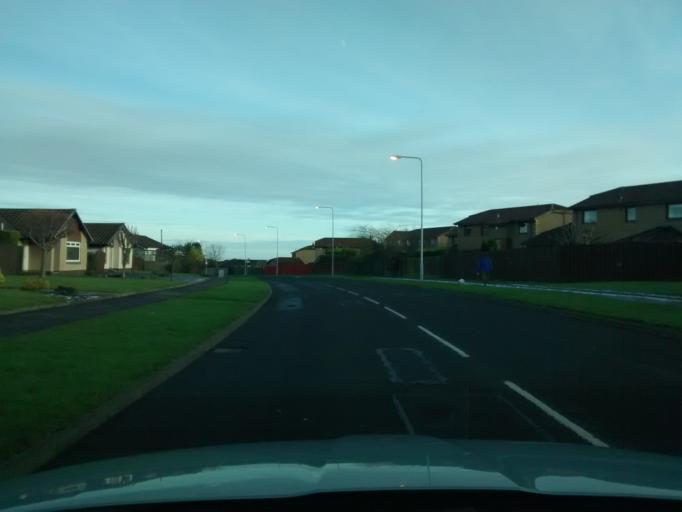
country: GB
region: Scotland
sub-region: Fife
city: Inverkeithing
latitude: 56.0286
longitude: -3.3609
